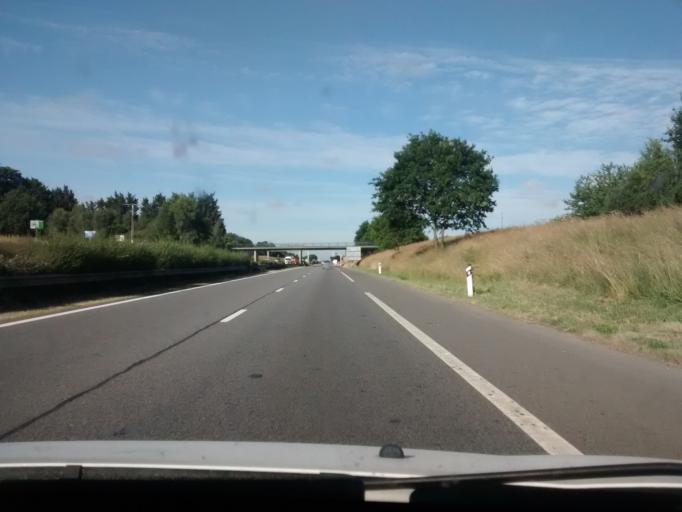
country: FR
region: Brittany
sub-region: Departement d'Ille-et-Vilaine
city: Chantepie
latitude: 48.0974
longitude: -1.6176
